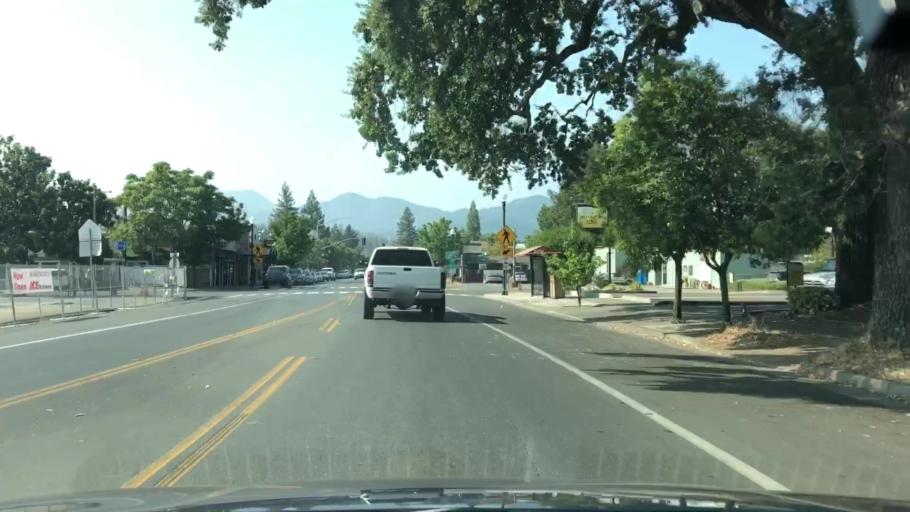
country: US
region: California
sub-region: Lake County
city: Middletown
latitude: 38.7536
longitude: -122.6148
